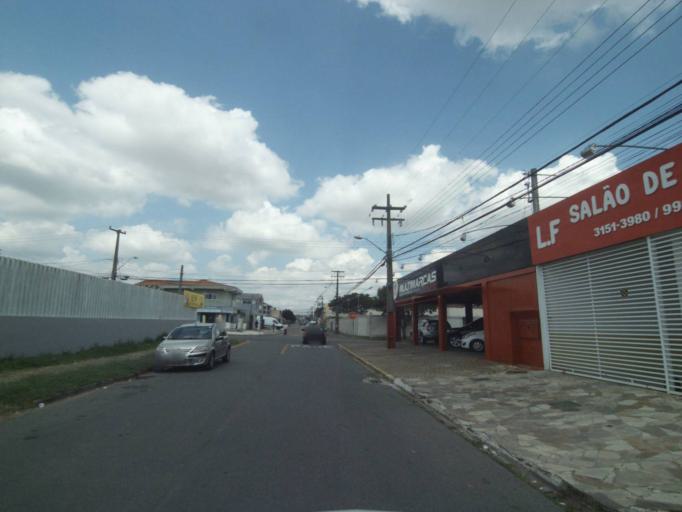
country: BR
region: Parana
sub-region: Sao Jose Dos Pinhais
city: Sao Jose dos Pinhais
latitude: -25.5356
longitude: -49.2567
